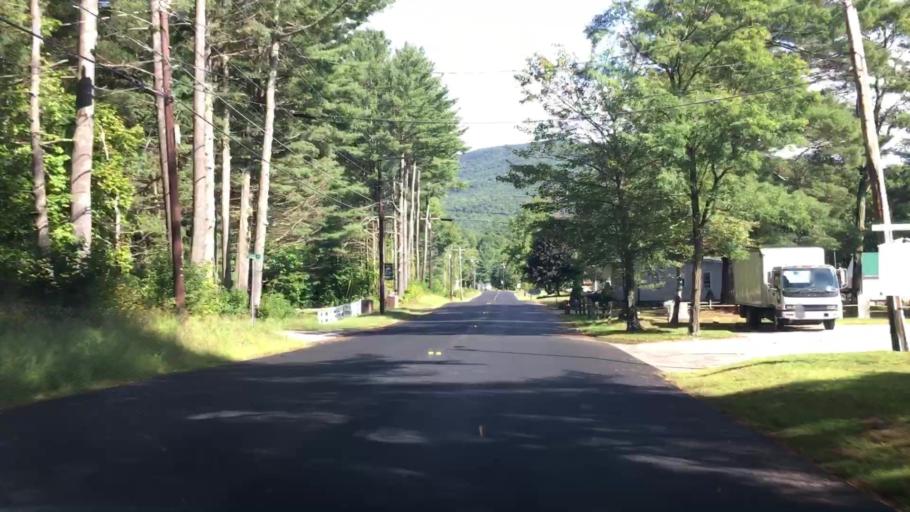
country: US
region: New Hampshire
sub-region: Grafton County
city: Woodstock
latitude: 44.0325
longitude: -71.6969
